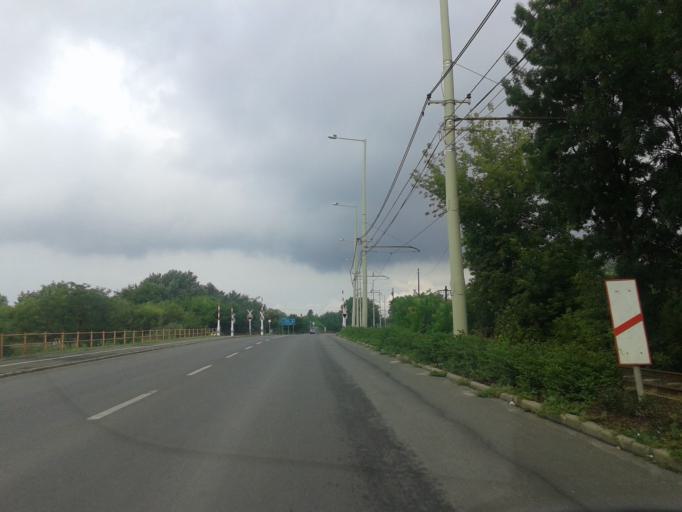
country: HU
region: Csongrad
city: Szeged
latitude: 46.2542
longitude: 20.1146
